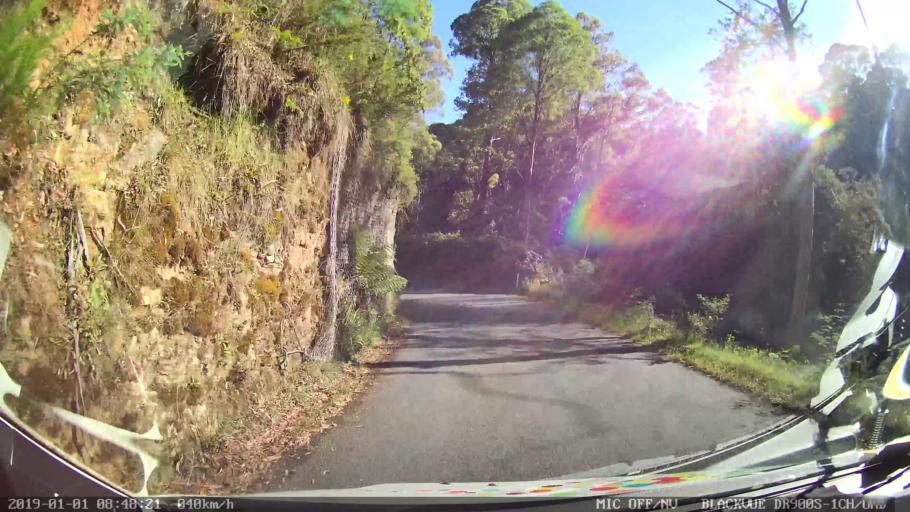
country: AU
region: New South Wales
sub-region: Snowy River
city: Jindabyne
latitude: -36.2892
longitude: 148.1995
